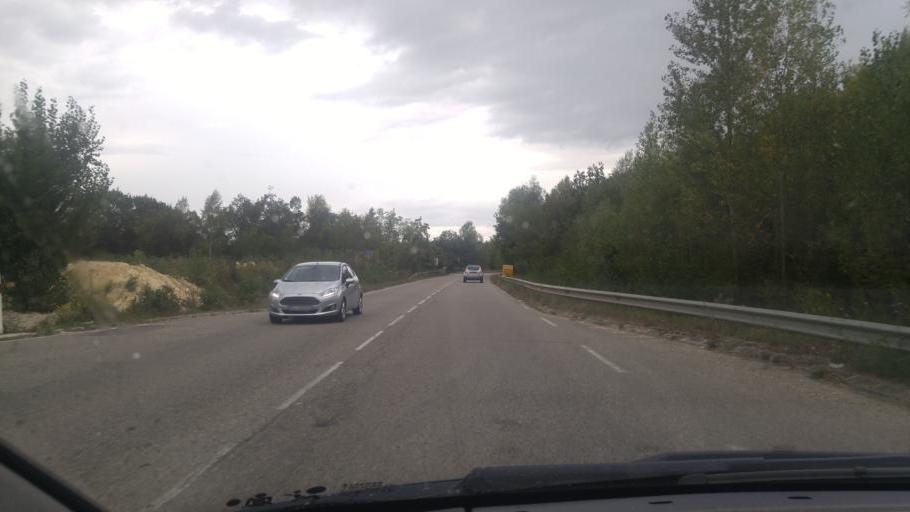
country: FR
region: Midi-Pyrenees
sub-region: Departement du Gers
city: Lectoure
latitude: 43.9178
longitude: 0.6267
